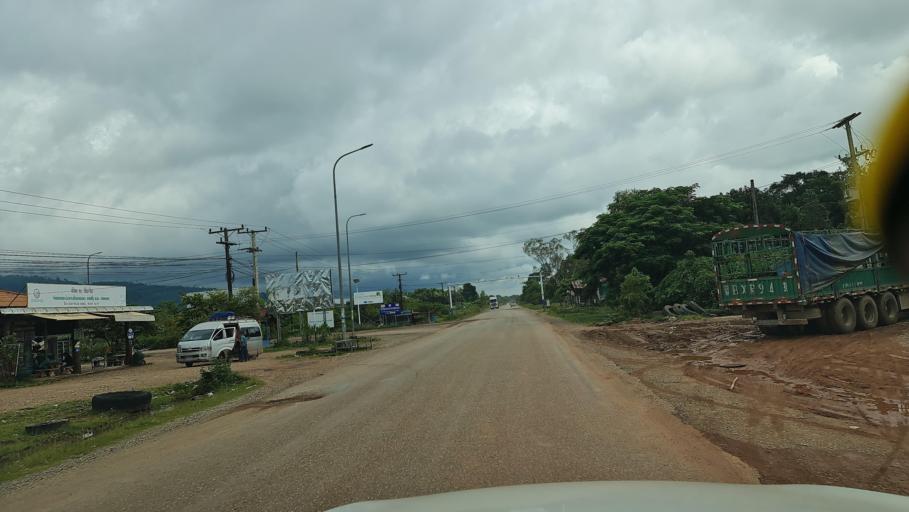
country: TH
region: Nong Khai
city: Rattanawapi
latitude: 18.1986
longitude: 103.0587
